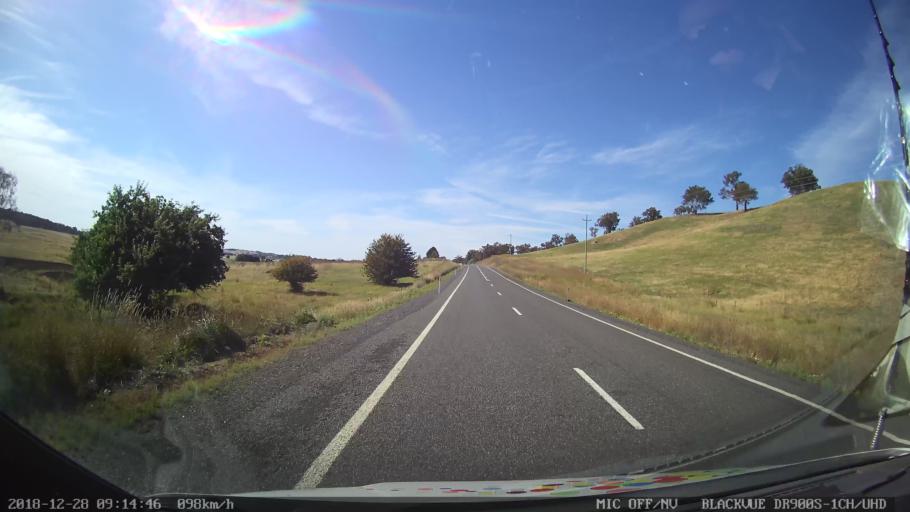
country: AU
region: New South Wales
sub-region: Upper Lachlan Shire
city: Crookwell
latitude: -34.2870
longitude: 149.3464
